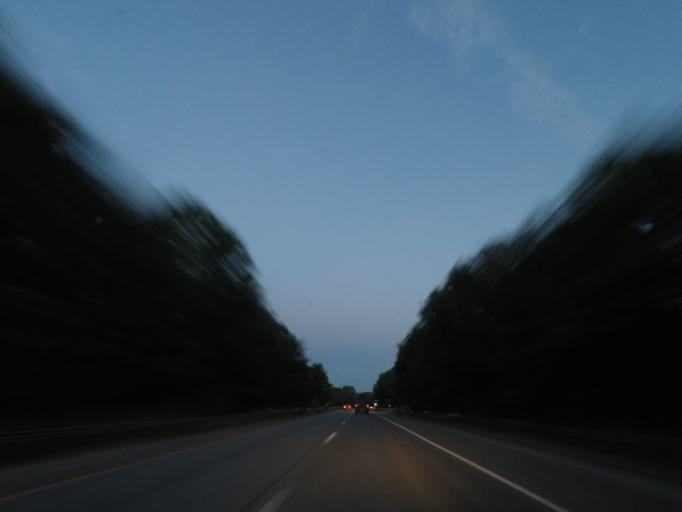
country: US
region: Connecticut
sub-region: Windham County
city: Putnam
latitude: 41.8954
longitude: -71.8976
